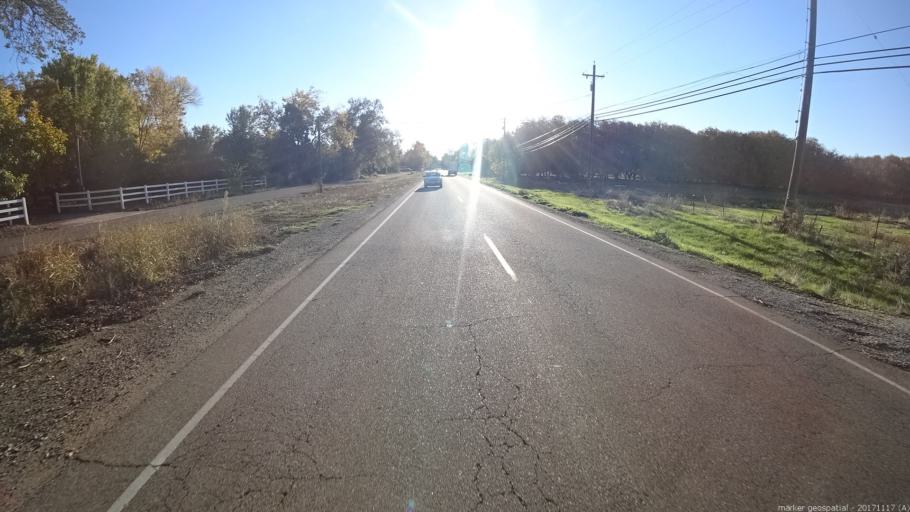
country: US
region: California
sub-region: Shasta County
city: Anderson
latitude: 40.4498
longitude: -122.2552
